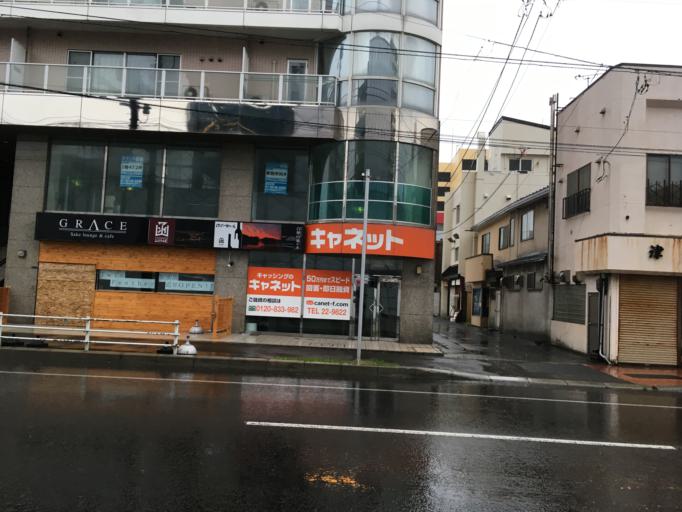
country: JP
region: Hokkaido
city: Hakodate
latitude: 41.7728
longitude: 140.7300
